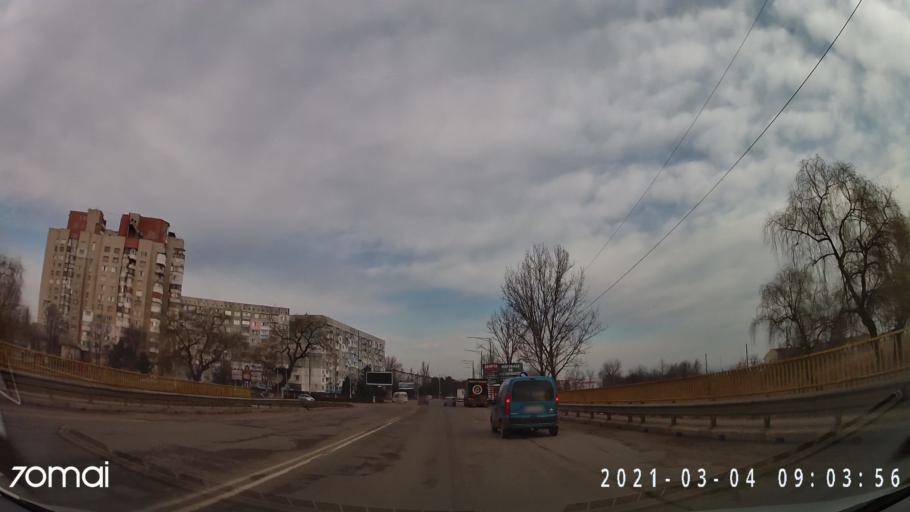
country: MD
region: Balti
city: Balti
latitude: 47.7547
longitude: 27.9421
